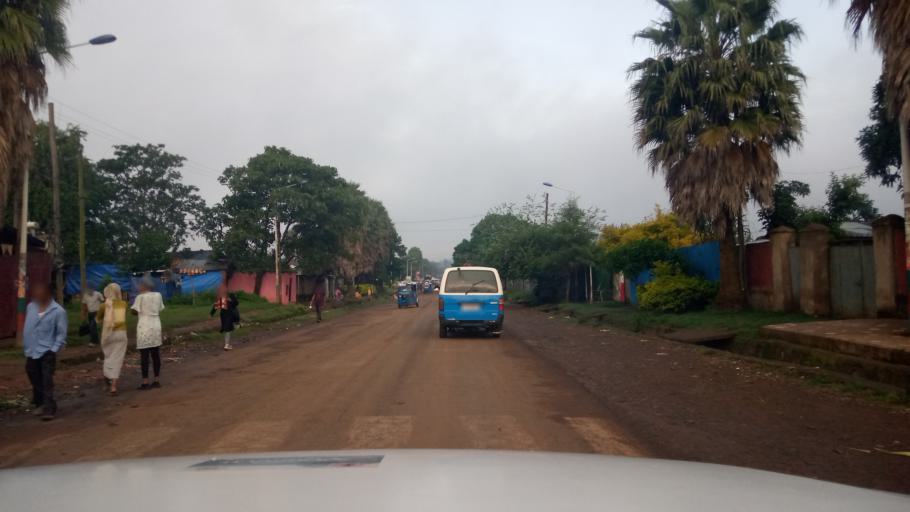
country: ET
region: Oromiya
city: Jima
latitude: 7.6843
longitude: 36.8472
